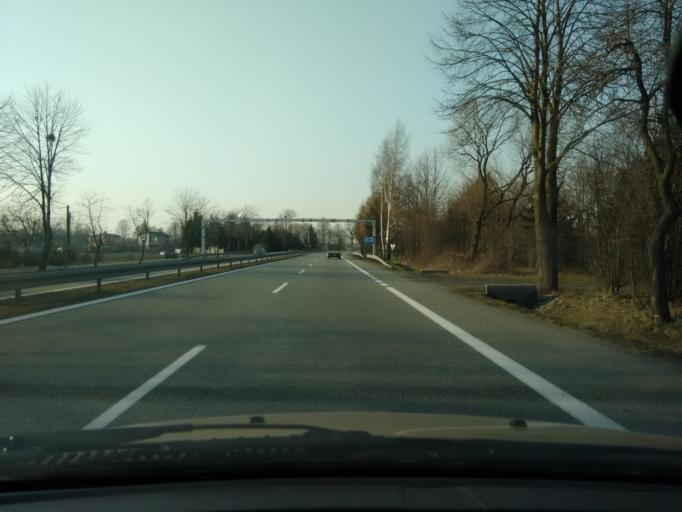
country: PL
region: Silesian Voivodeship
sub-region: Powiat cieszynski
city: Drogomysl
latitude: 49.8698
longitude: 18.7455
